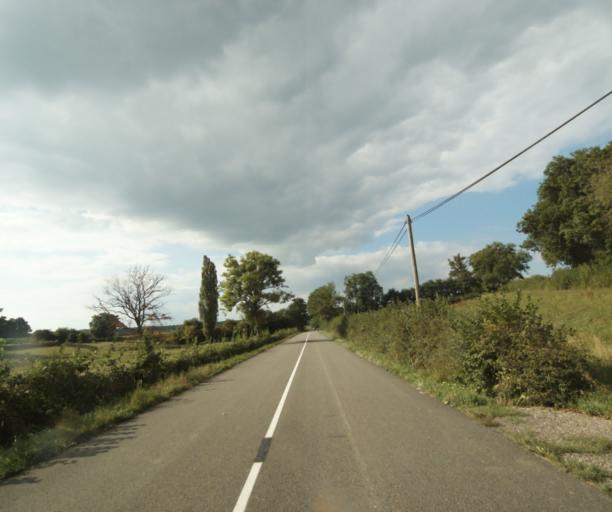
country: FR
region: Bourgogne
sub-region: Departement de Saone-et-Loire
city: Palinges
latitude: 46.5125
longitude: 4.2583
